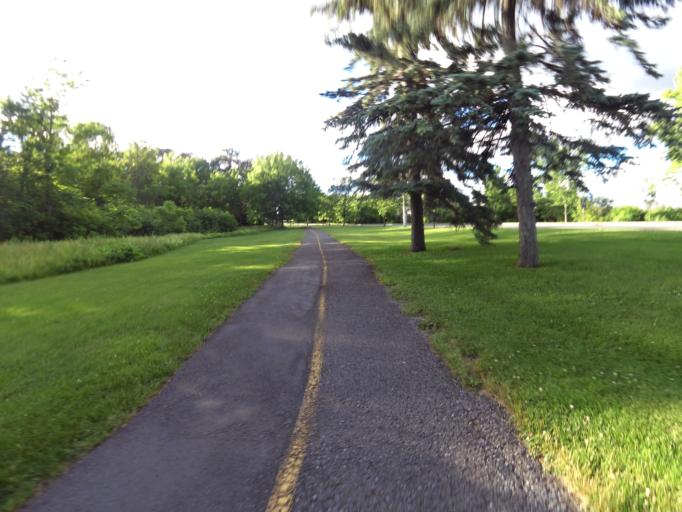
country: CA
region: Ontario
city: Ottawa
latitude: 45.3867
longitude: -75.7246
